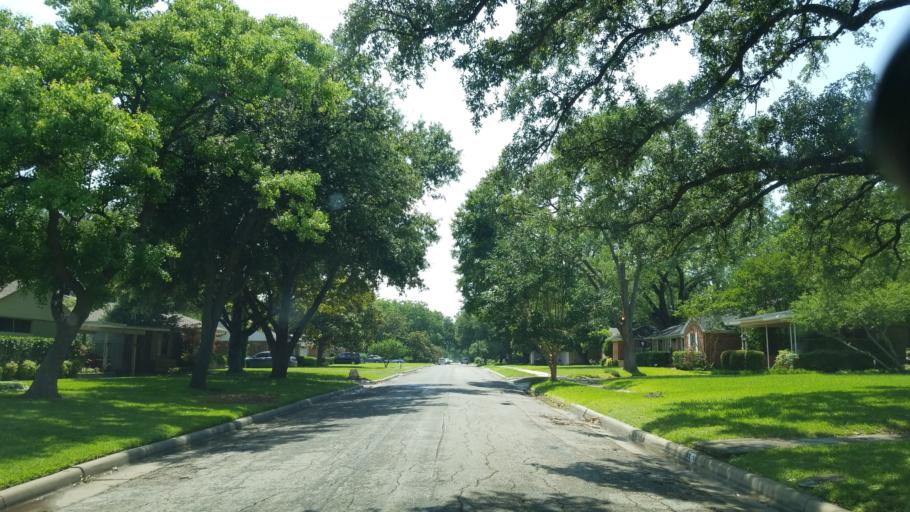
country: US
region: Texas
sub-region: Dallas County
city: Farmers Branch
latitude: 32.8790
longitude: -96.8651
